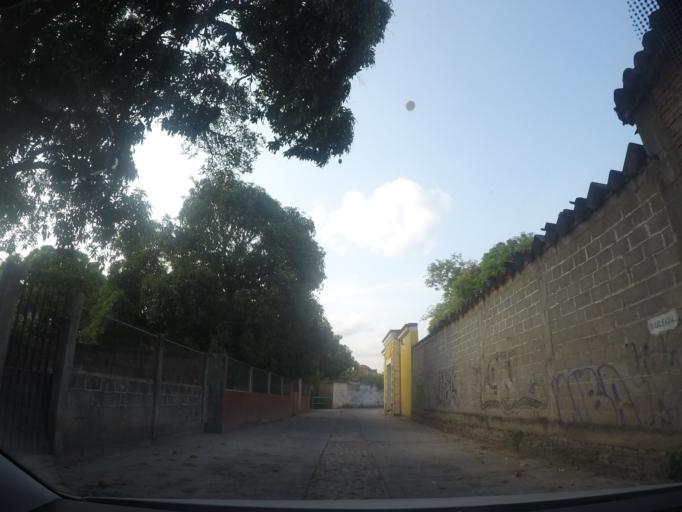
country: MX
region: Oaxaca
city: San Jeronimo Ixtepec
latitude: 16.5910
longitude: -95.1613
